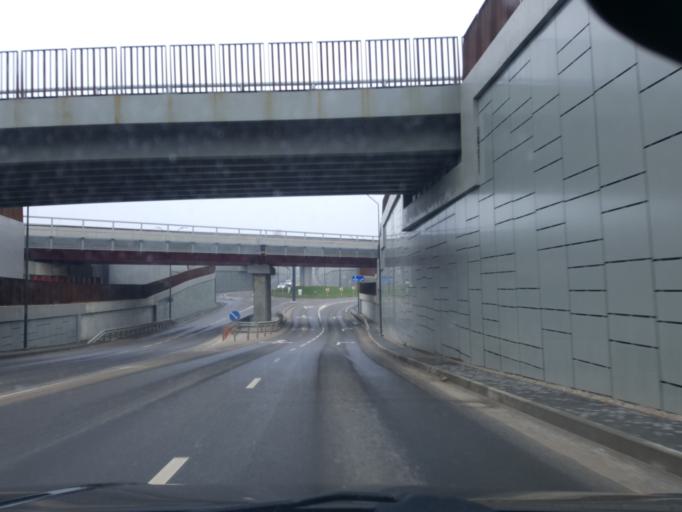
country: LT
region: Marijampoles apskritis
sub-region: Marijampole Municipality
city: Marijampole
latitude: 54.5376
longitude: 23.3513
